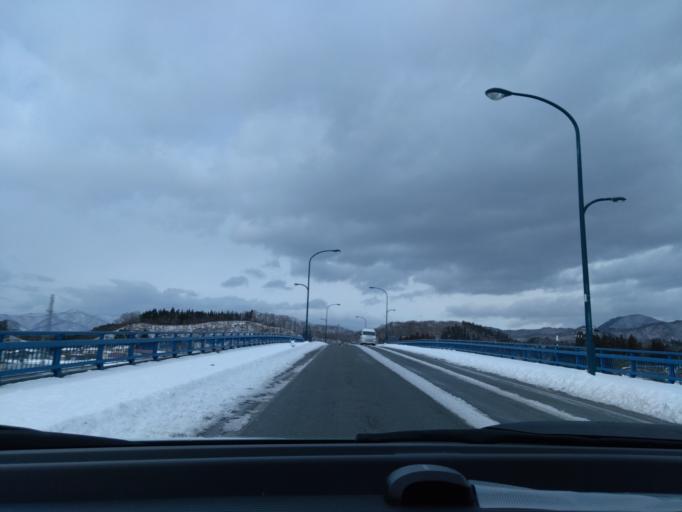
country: JP
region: Akita
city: Kakunodatemachi
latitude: 39.6228
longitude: 140.6302
